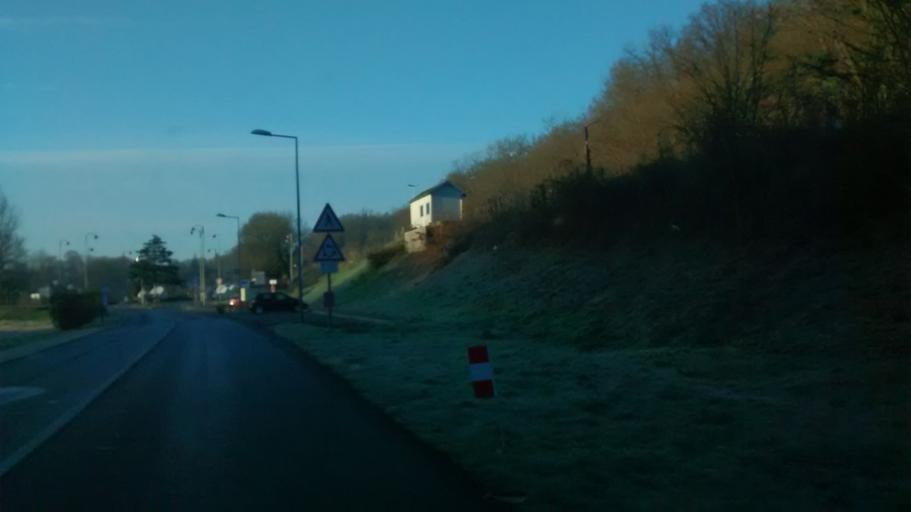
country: FR
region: Centre
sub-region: Departement d'Indre-et-Loire
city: Veigne
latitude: 47.2918
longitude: 0.7358
